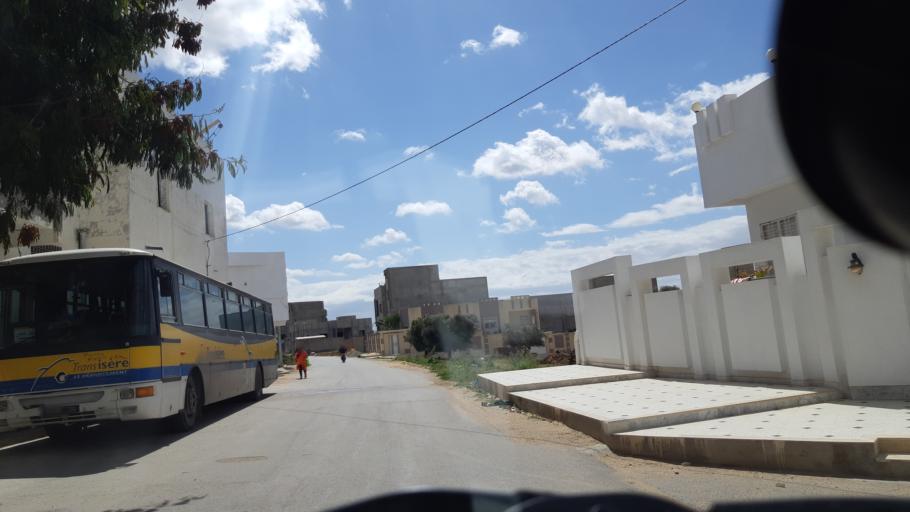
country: TN
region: Susah
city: Akouda
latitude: 35.8806
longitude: 10.5404
